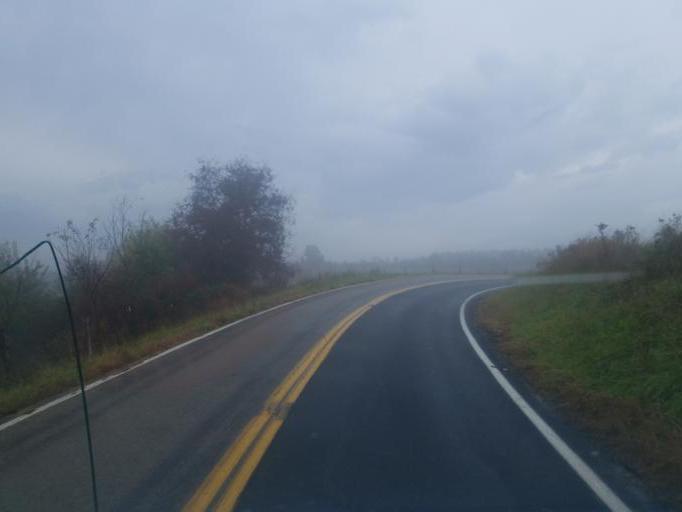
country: US
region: Ohio
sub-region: Athens County
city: Glouster
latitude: 39.5258
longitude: -81.9387
